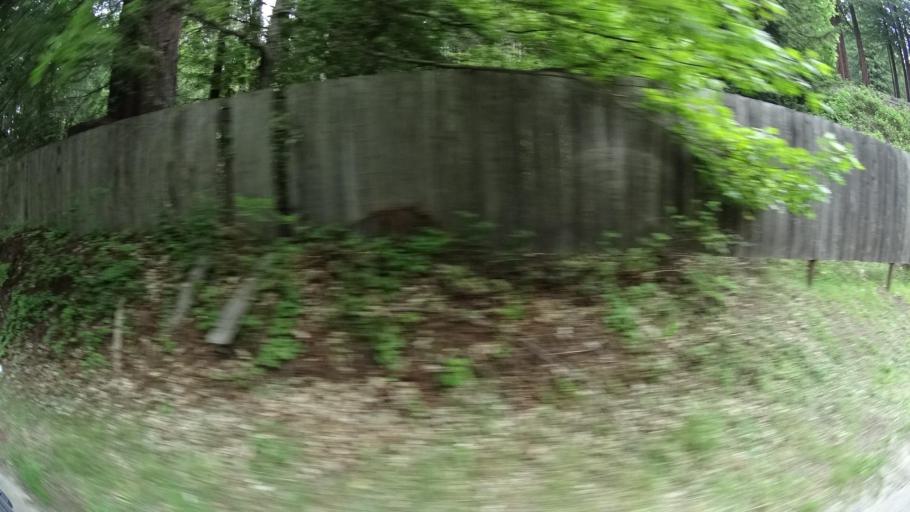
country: US
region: California
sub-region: Humboldt County
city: Redway
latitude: 40.1270
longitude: -123.8517
